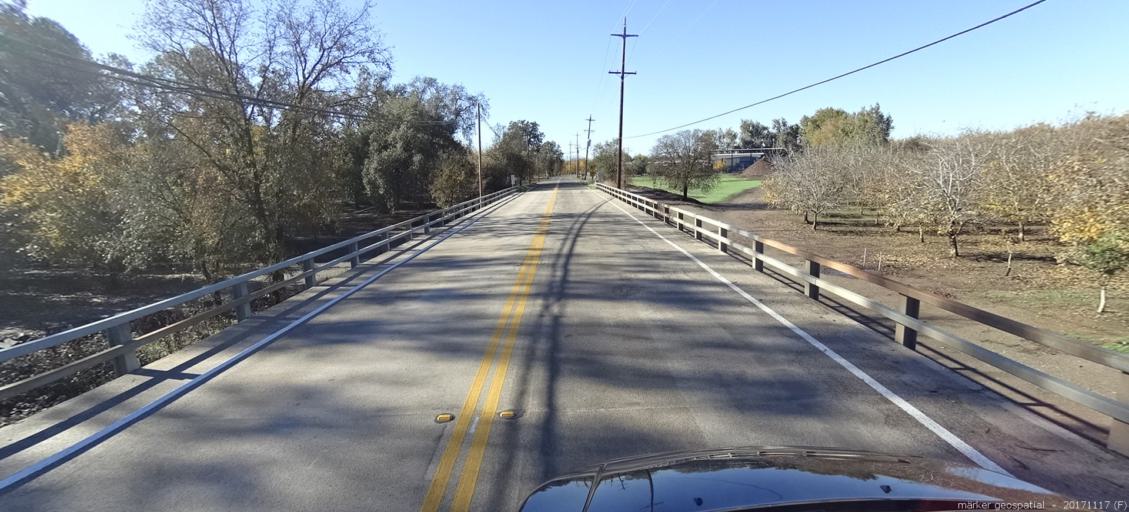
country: US
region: California
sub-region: Shasta County
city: Cottonwood
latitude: 40.4156
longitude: -122.1995
